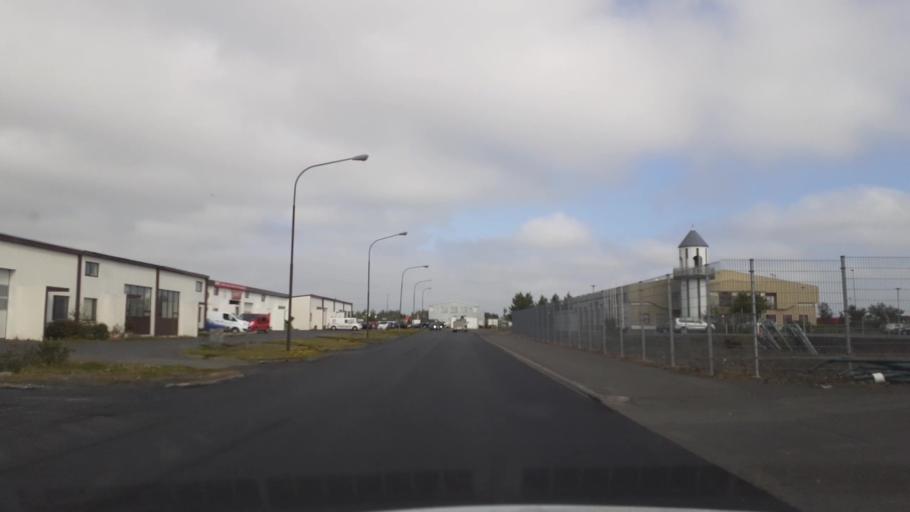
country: IS
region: Capital Region
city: Hafnarfjoerdur
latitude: 64.0802
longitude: -21.9364
